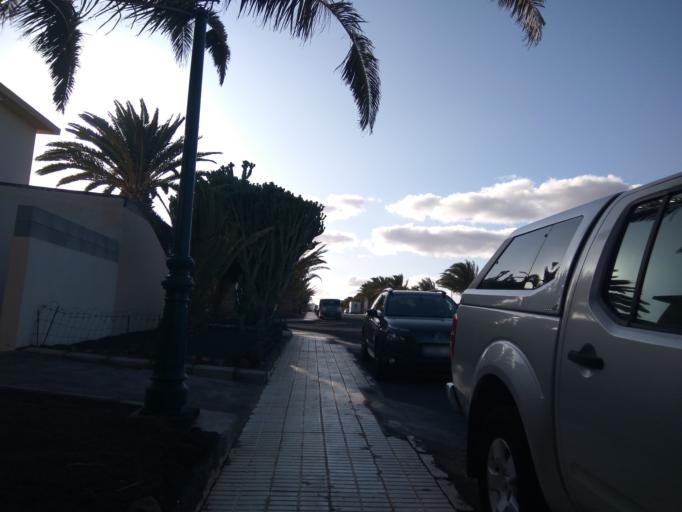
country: ES
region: Canary Islands
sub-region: Provincia de Las Palmas
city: Arrecife
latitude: 29.0073
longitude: -13.4885
